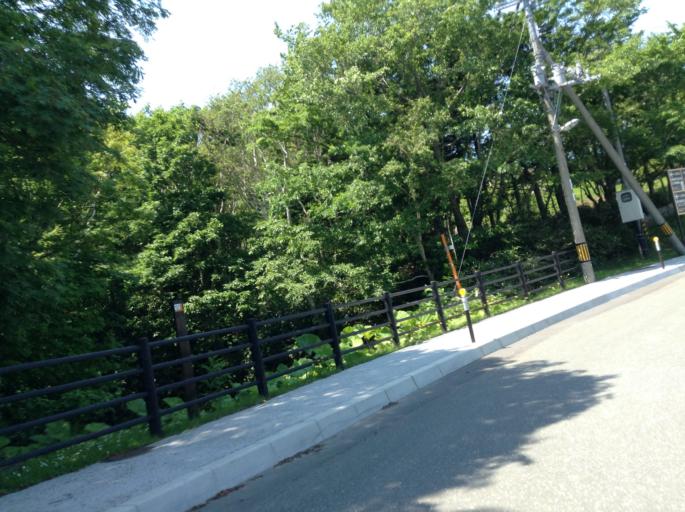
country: JP
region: Hokkaido
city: Wakkanai
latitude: 45.4196
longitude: 141.6690
